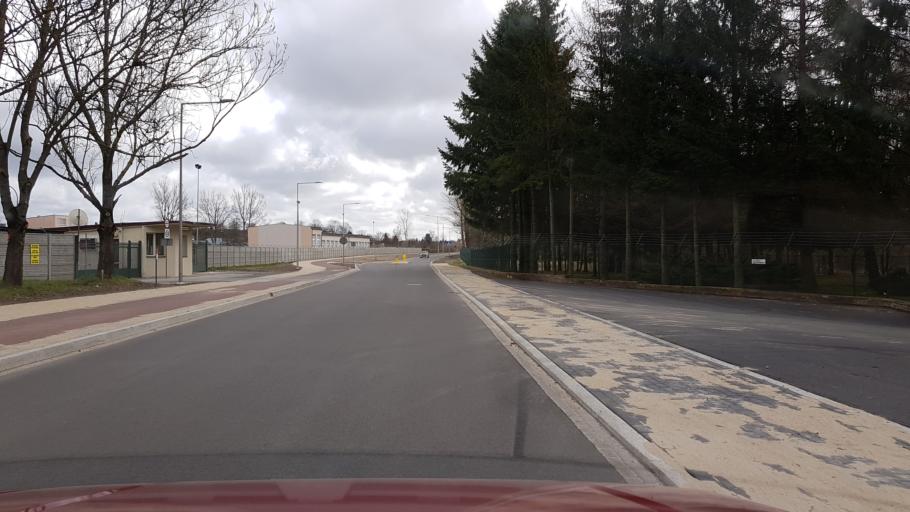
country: PL
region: West Pomeranian Voivodeship
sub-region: Koszalin
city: Koszalin
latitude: 54.1828
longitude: 16.2104
